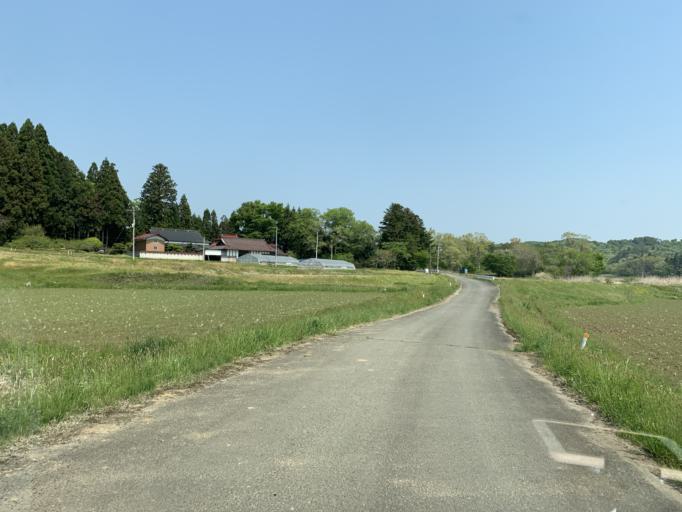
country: JP
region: Iwate
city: Ichinoseki
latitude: 38.8568
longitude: 141.0653
